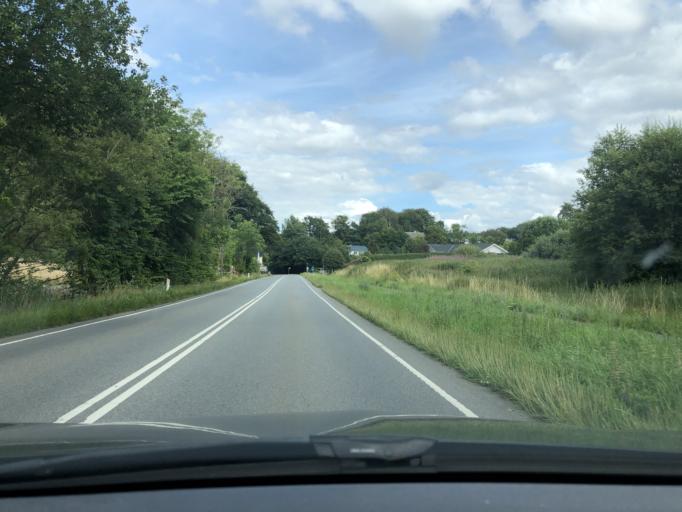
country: DK
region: South Denmark
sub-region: Vejle Kommune
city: Vejle
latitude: 55.6930
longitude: 9.4819
